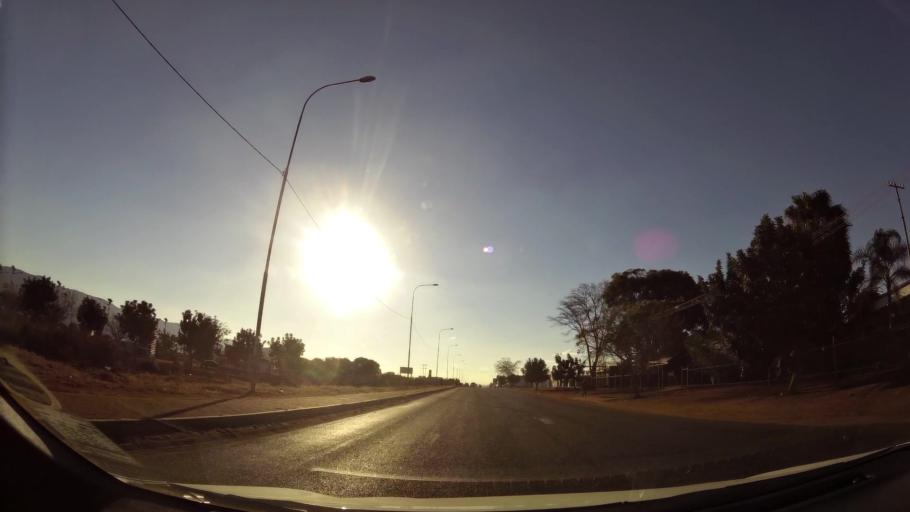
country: ZA
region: Limpopo
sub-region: Waterberg District Municipality
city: Mokopane
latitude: -24.1678
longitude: 28.9960
